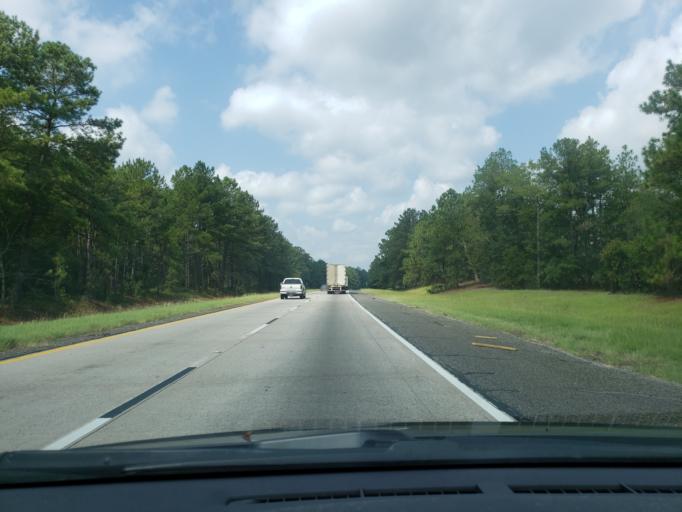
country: US
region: Georgia
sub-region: Treutlen County
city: Soperton
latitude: 32.4278
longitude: -82.5353
